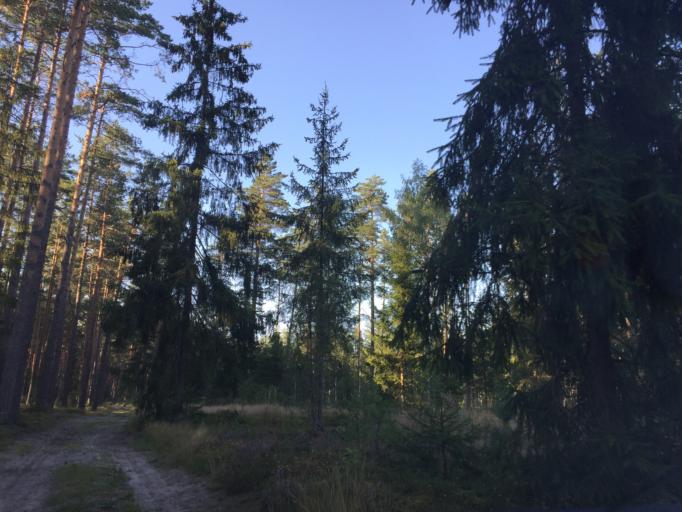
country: LV
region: Garkalne
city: Garkalne
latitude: 57.0105
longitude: 24.4407
